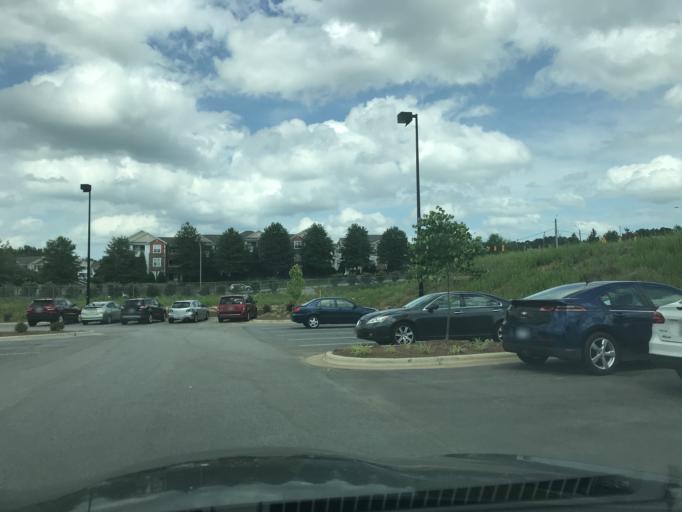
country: US
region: North Carolina
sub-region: Wake County
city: Wake Forest
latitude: 35.9462
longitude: -78.5071
